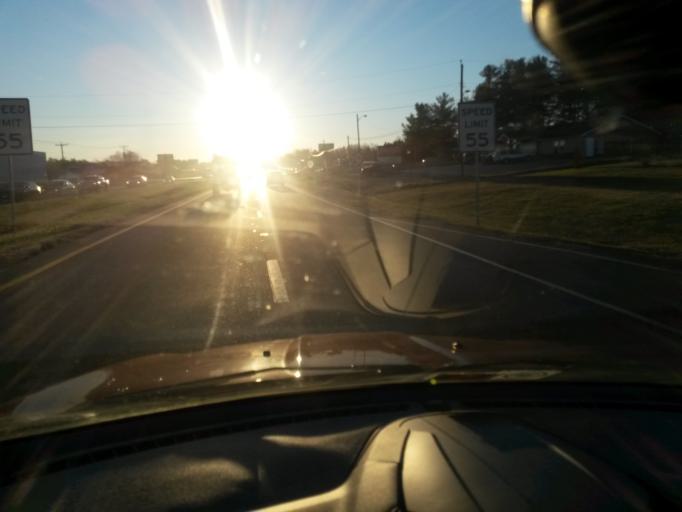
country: US
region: Virginia
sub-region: Franklin County
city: Rocky Mount
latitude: 37.0708
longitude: -79.8961
